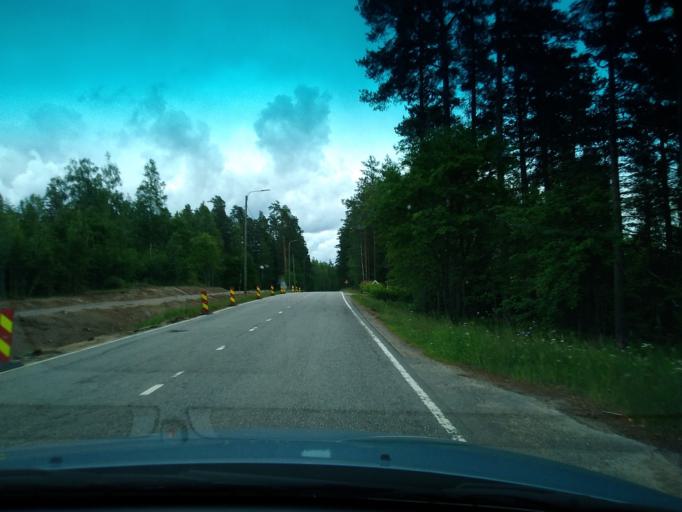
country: FI
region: Central Finland
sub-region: Keuruu
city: Multia
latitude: 62.4138
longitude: 24.7919
